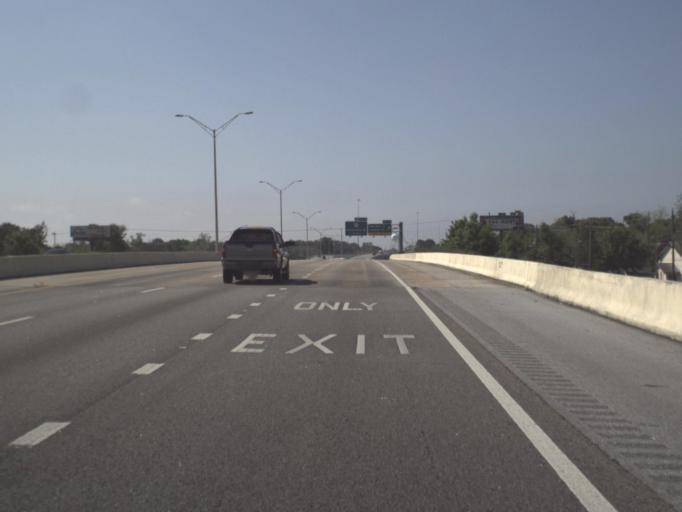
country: US
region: Florida
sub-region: Escambia County
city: Goulding
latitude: 30.4407
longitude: -87.2167
